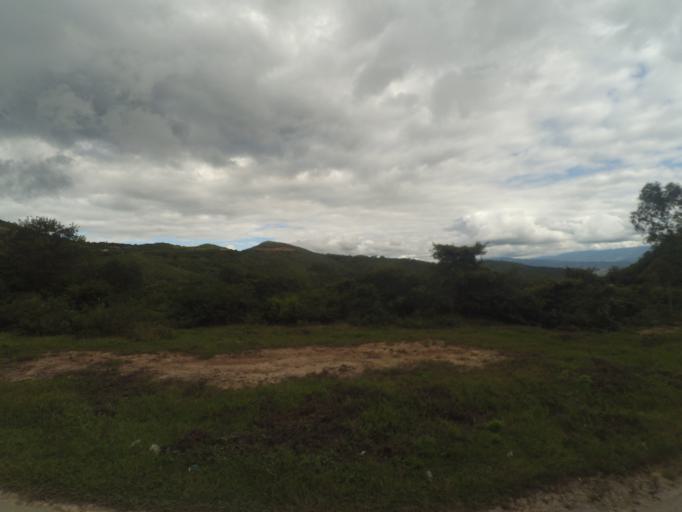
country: BO
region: Santa Cruz
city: Samaipata
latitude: -18.1748
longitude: -63.8736
